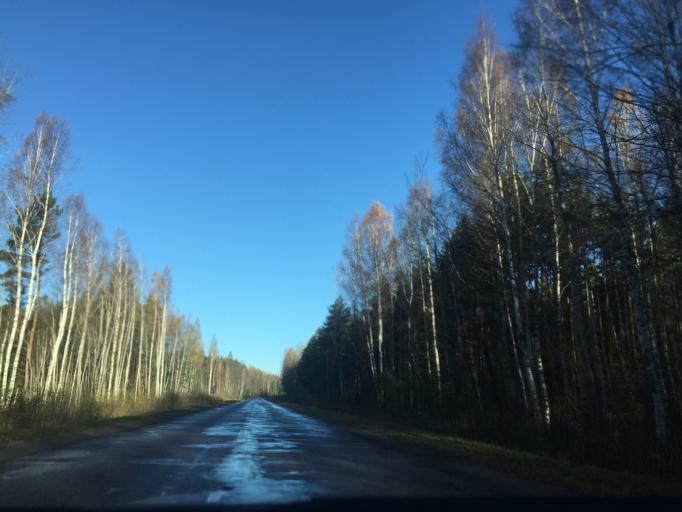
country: LV
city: Tireli
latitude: 56.9139
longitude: 23.5257
